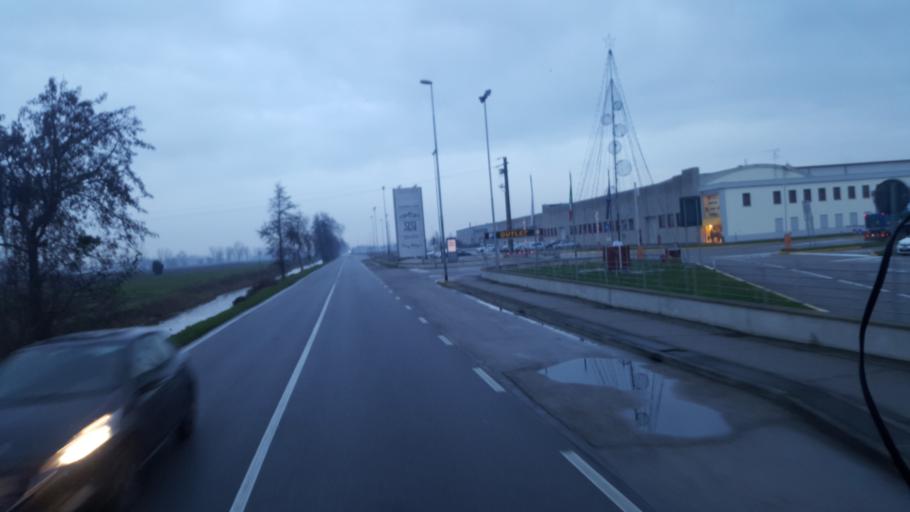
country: IT
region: Lombardy
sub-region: Provincia di Mantova
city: Casalmoro
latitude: 45.2651
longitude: 10.4144
